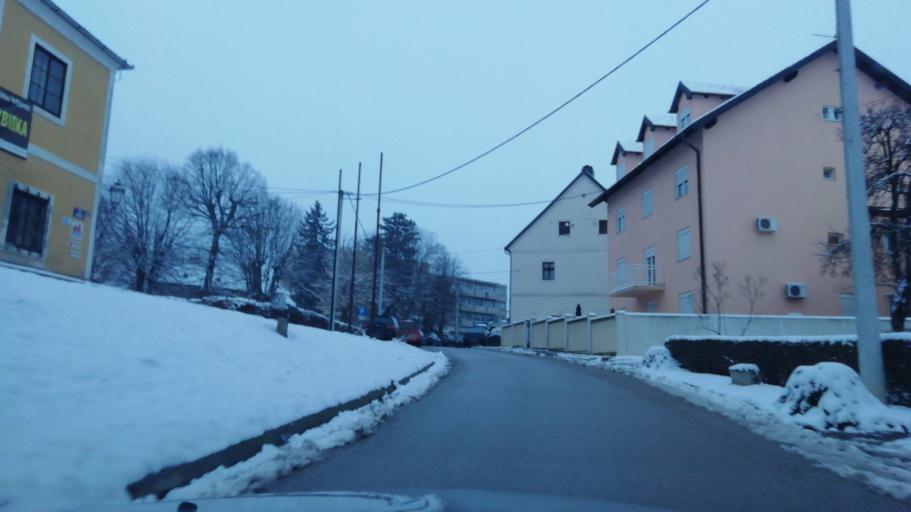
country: HR
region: Zagrebacka
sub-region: Grad Vrbovec
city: Vrbovec
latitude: 45.8840
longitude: 16.4177
